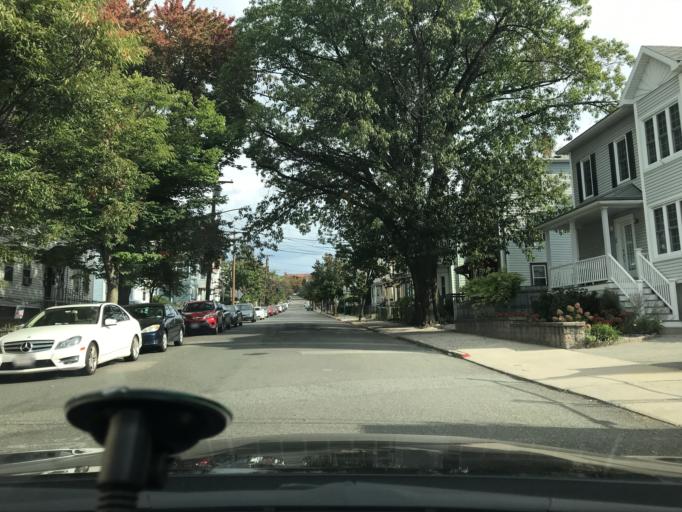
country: US
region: Massachusetts
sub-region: Middlesex County
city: Somerville
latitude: 42.3838
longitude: -71.0997
